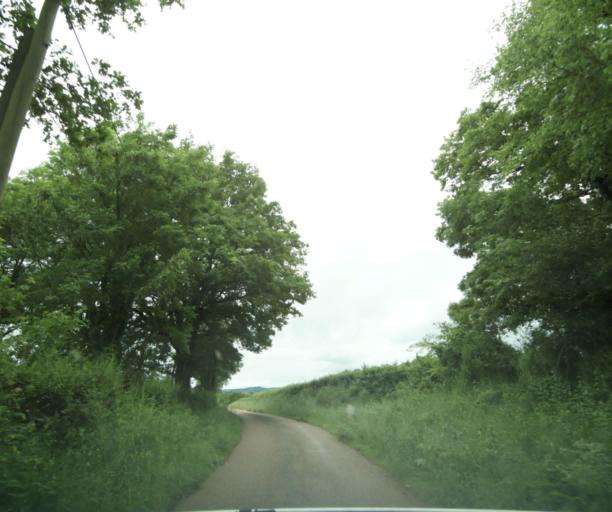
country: FR
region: Bourgogne
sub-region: Departement de Saone-et-Loire
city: Charolles
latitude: 46.4723
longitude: 4.3512
